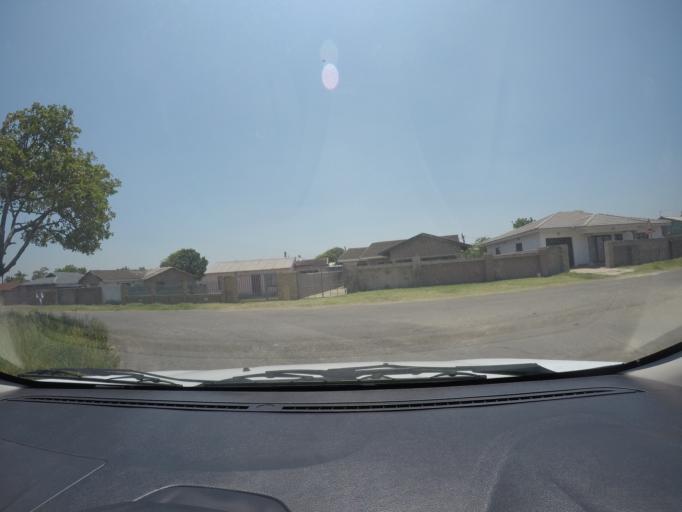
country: ZA
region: KwaZulu-Natal
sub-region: uThungulu District Municipality
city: eSikhawini
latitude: -28.8854
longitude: 31.8886
